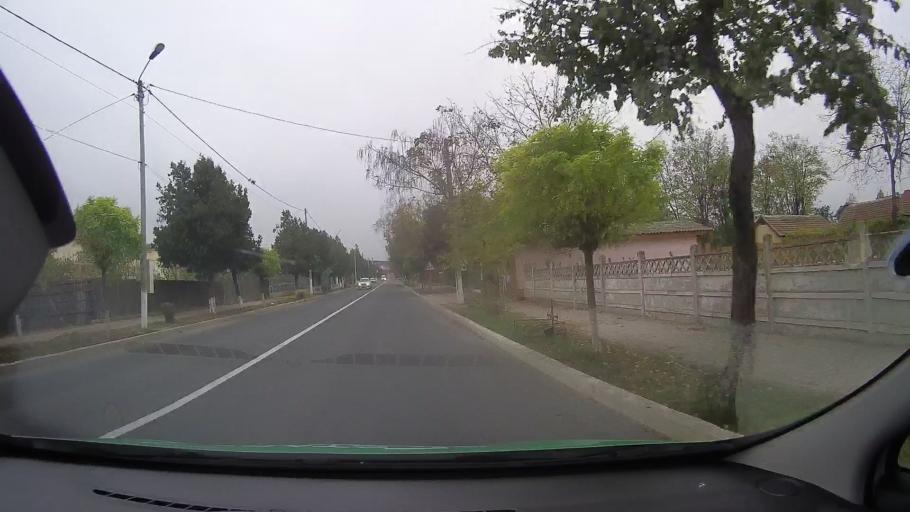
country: RO
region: Constanta
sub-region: Oras Harsova
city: Harsova
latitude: 44.6874
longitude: 27.9539
